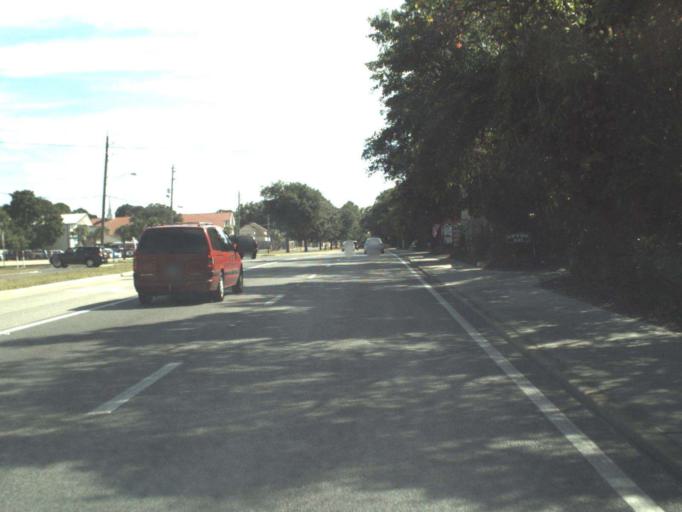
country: US
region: Florida
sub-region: Okaloosa County
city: Mary Esther
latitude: 30.4101
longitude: -86.6788
